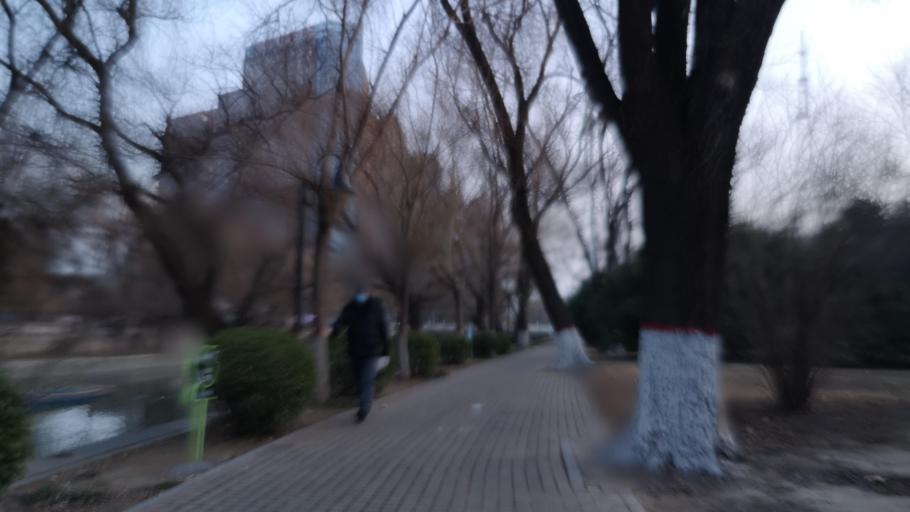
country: CN
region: Henan Sheng
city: Zhongyuanlu
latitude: 35.7767
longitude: 115.0779
